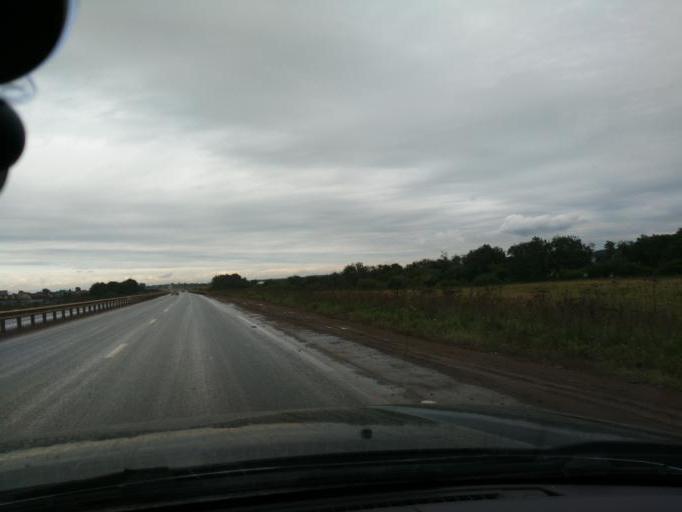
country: RU
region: Perm
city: Kultayevo
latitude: 57.8989
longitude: 55.9700
